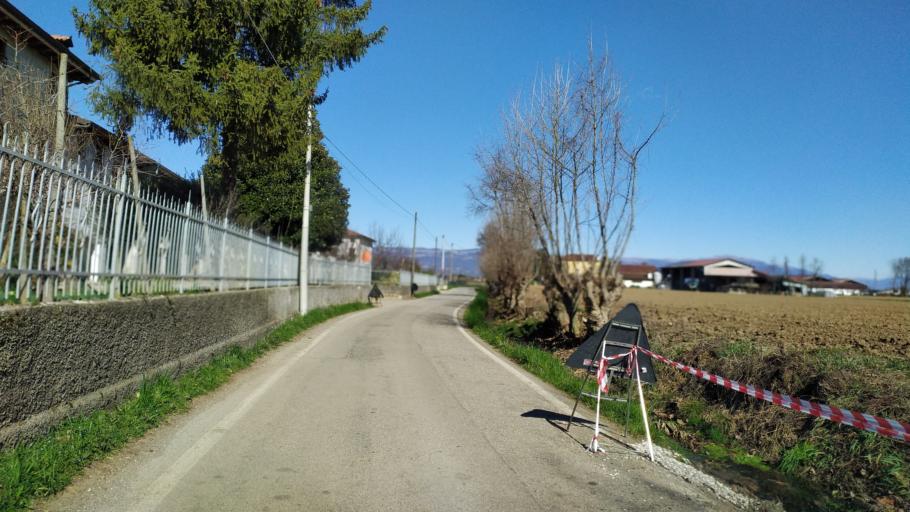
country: IT
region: Veneto
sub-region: Provincia di Vicenza
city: Vigardolo
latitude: 45.6215
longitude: 11.5854
